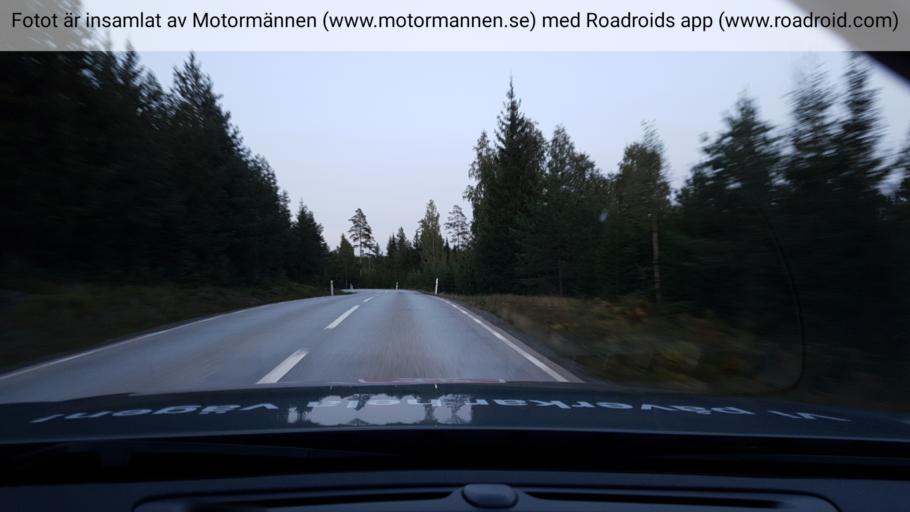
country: SE
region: OErebro
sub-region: Ljusnarsbergs Kommun
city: Kopparberg
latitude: 59.8041
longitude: 14.8618
